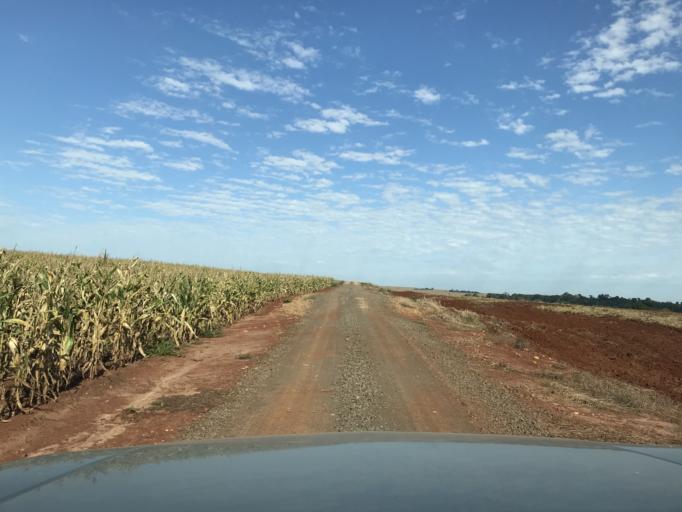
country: BR
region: Parana
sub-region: Palotina
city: Palotina
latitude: -24.1594
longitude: -53.7443
